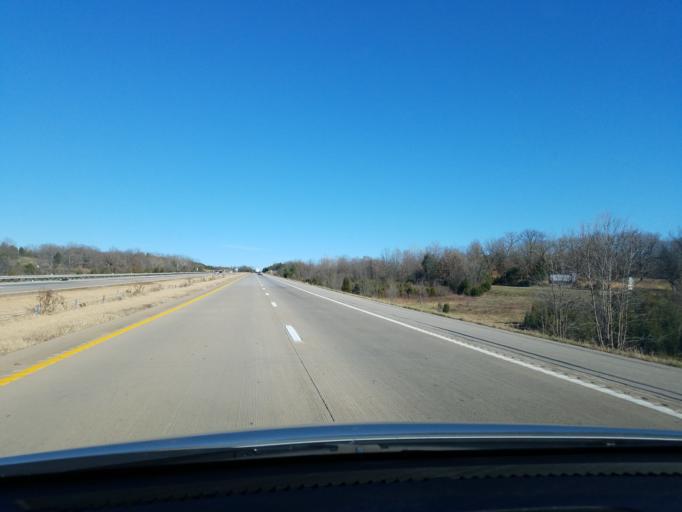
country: US
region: Missouri
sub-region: Pulaski County
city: Richland
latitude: 37.7640
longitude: -92.4447
